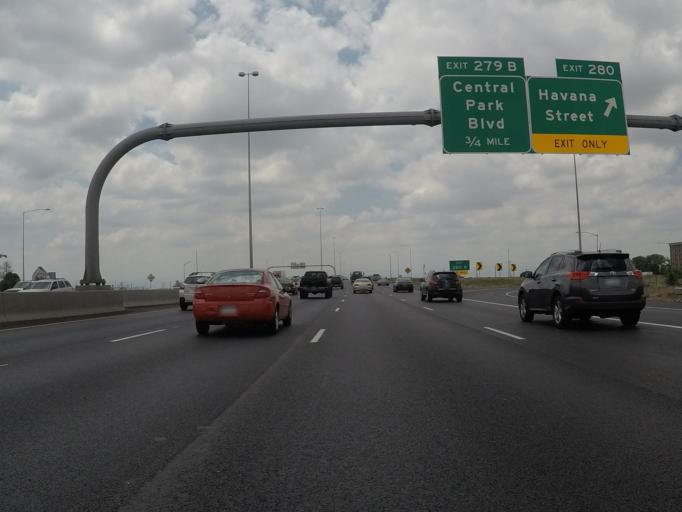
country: US
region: Colorado
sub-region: Adams County
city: Aurora
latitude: 39.7755
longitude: -104.8618
